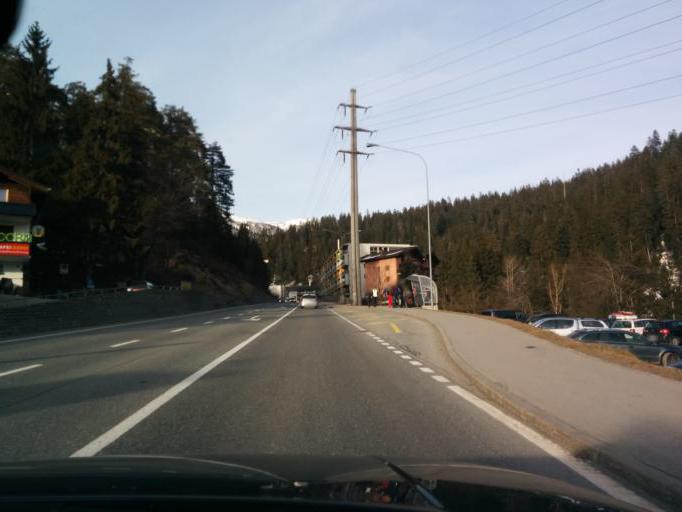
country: CH
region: Grisons
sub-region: Surselva District
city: Laax
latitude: 46.8127
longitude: 9.2635
